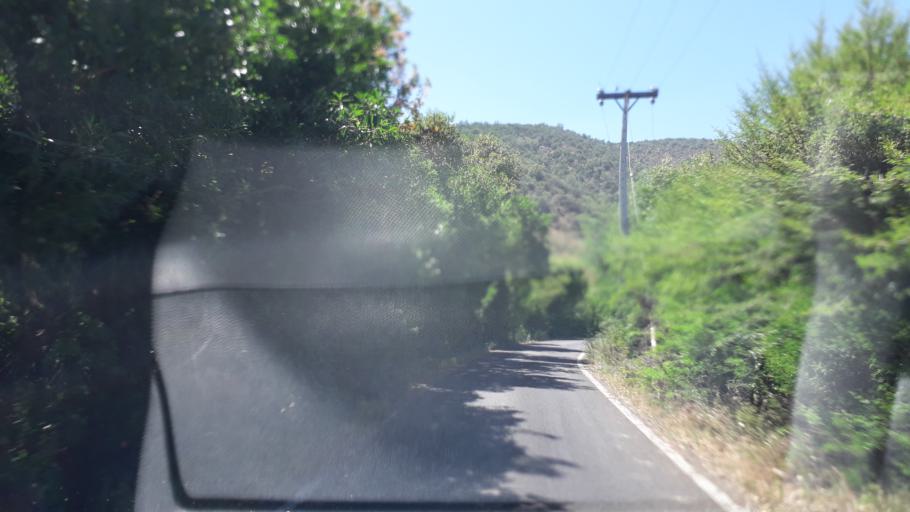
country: CL
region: Valparaiso
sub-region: Provincia de Marga Marga
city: Limache
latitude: -33.0745
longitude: -71.2119
